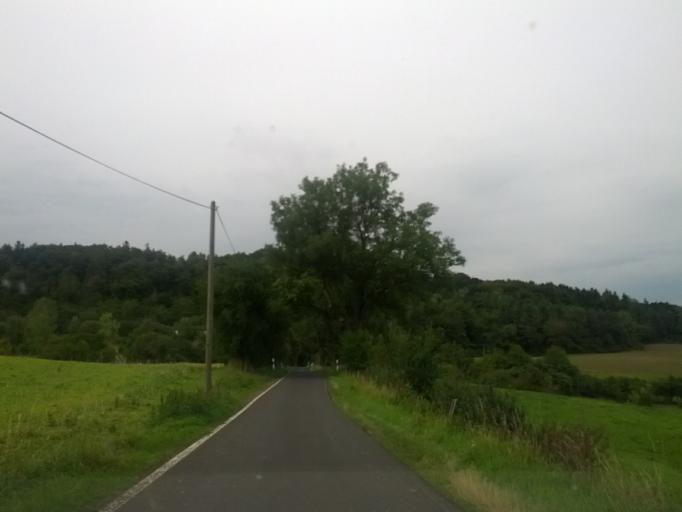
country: DE
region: Thuringia
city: Wolfsburg-Unkeroda
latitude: 50.9030
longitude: 10.2585
